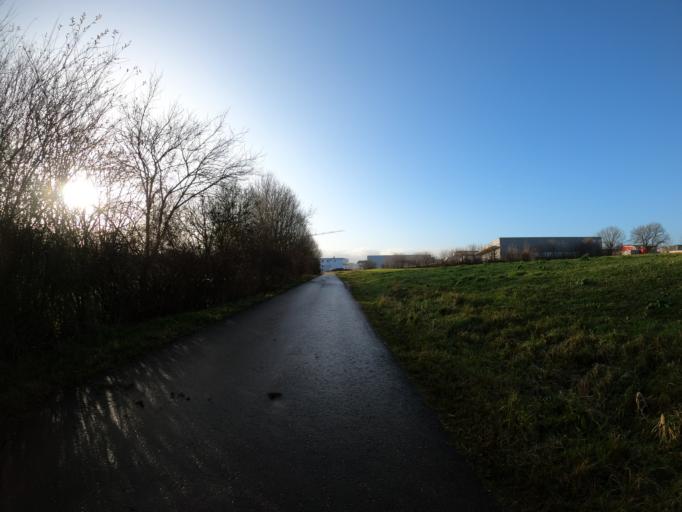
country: DE
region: Baden-Wuerttemberg
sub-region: Regierungsbezirk Stuttgart
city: Heiningen
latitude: 48.6792
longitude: 9.6268
